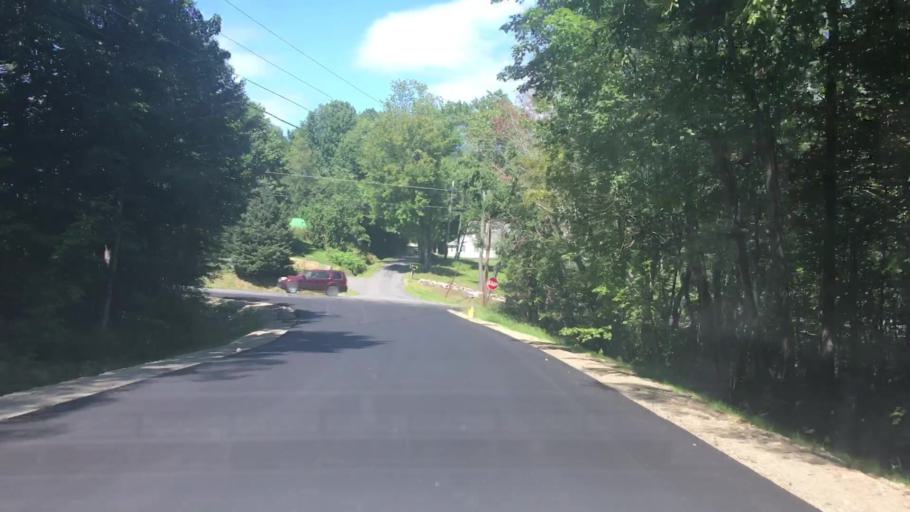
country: US
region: Maine
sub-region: Androscoggin County
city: Sabattus
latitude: 44.1345
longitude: -70.0196
